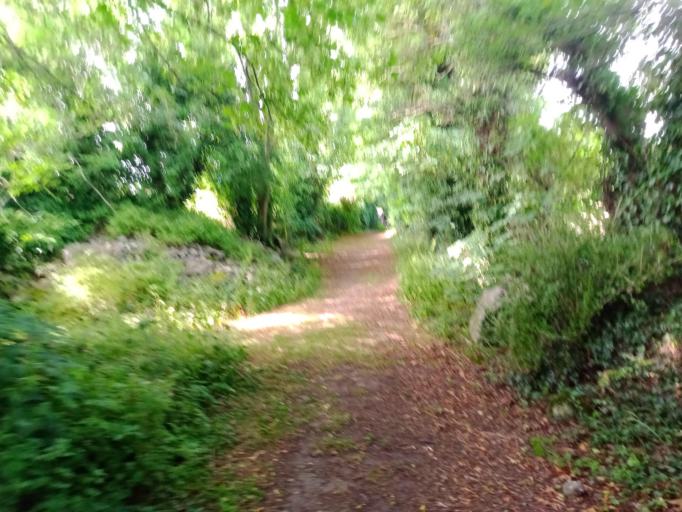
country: IE
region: Leinster
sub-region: Laois
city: Rathdowney
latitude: 52.8147
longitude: -7.4757
